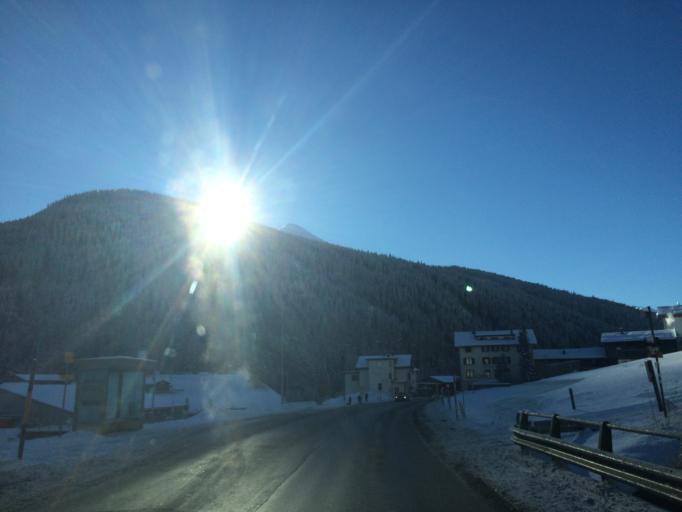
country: CH
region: Grisons
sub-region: Praettigau/Davos District
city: Davos
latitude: 46.7701
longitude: 9.8004
